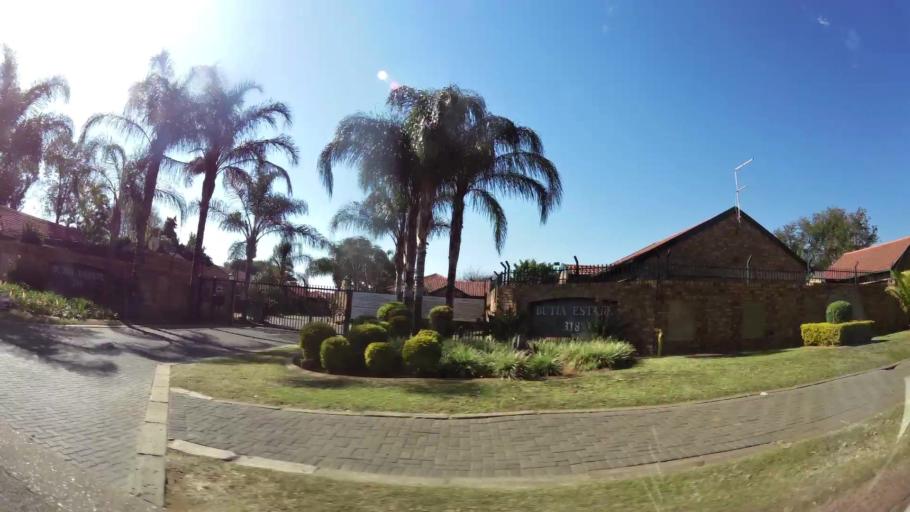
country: ZA
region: Gauteng
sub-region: City of Tshwane Metropolitan Municipality
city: Pretoria
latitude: -25.6766
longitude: 28.2375
